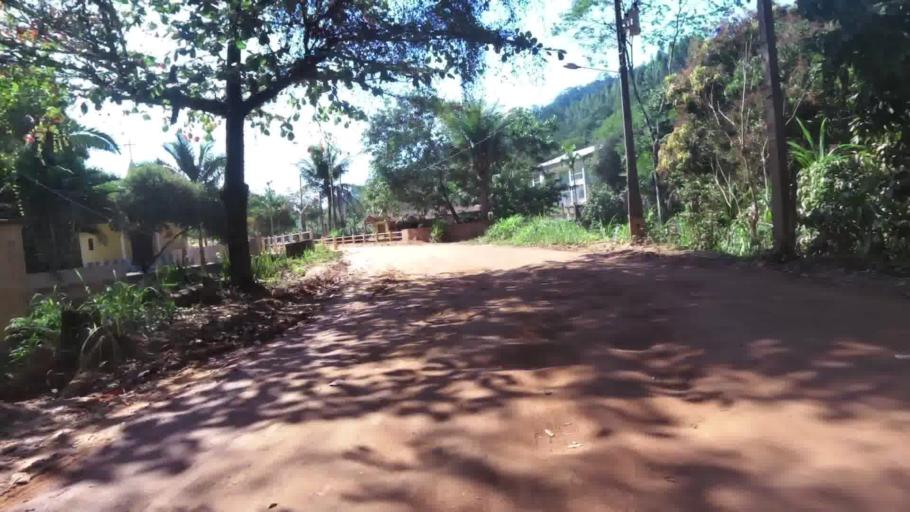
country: BR
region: Espirito Santo
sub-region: Alfredo Chaves
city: Alfredo Chaves
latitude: -20.6439
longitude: -40.7804
